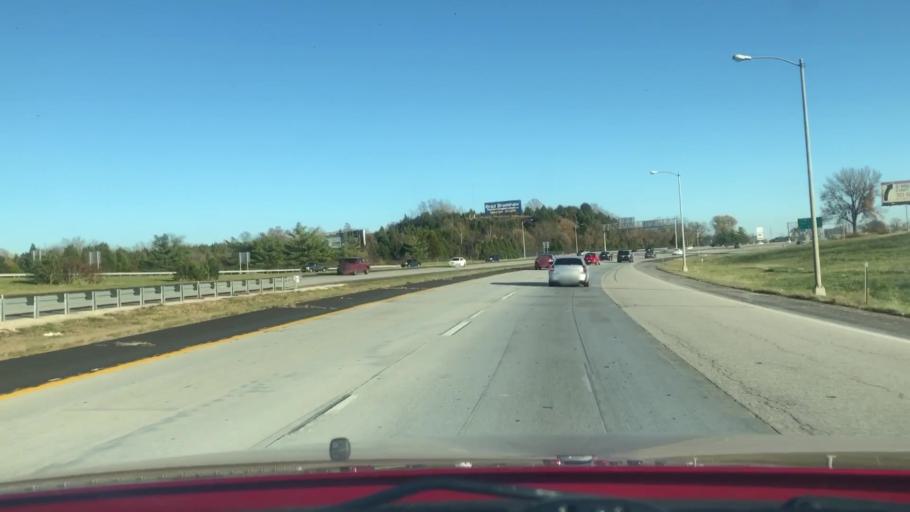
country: US
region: Missouri
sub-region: Greene County
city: Springfield
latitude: 37.1388
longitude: -93.2521
